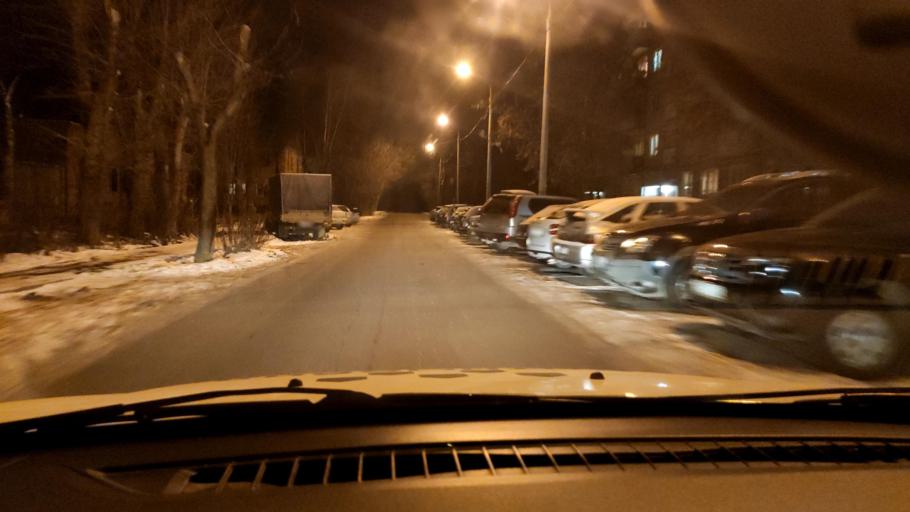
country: RU
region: Perm
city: Overyata
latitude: 58.0301
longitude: 55.8467
